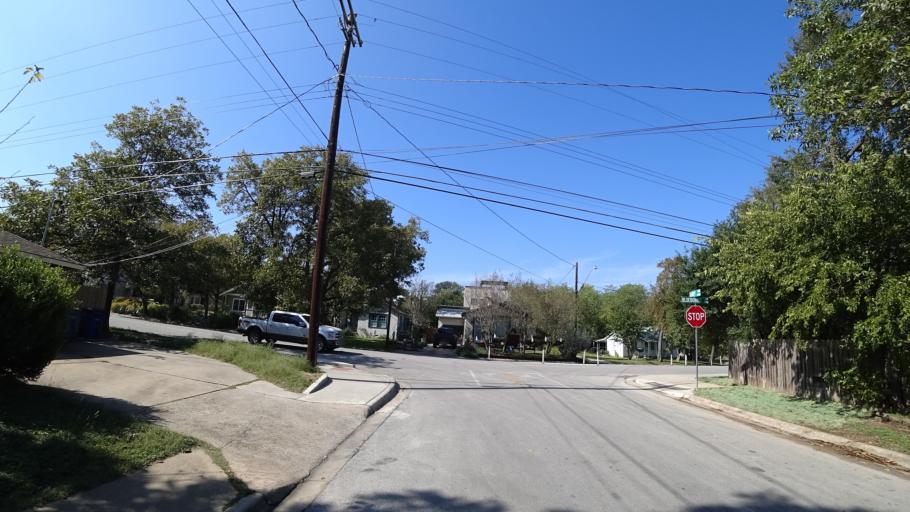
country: US
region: Texas
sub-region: Travis County
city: Rollingwood
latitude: 30.2562
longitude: -97.7709
